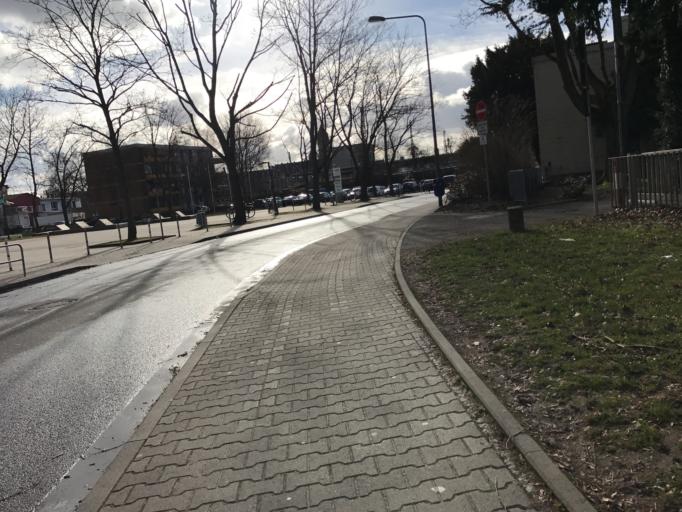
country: DE
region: Hesse
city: Sulzbach
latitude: 50.1041
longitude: 8.5421
